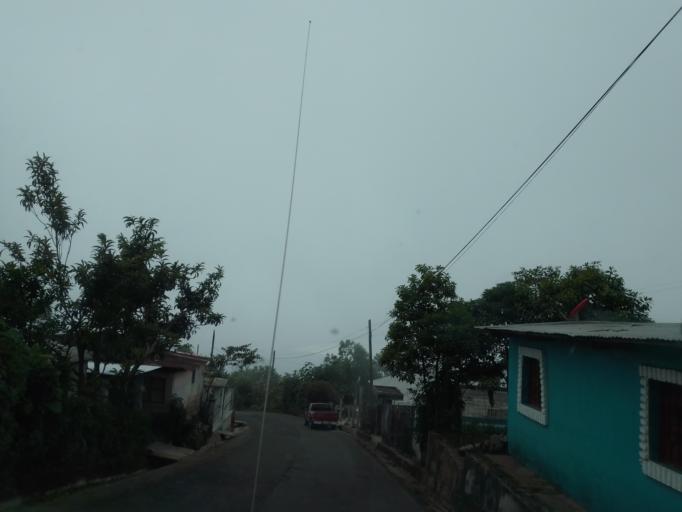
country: MX
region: Chiapas
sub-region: Union Juarez
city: Santo Domingo
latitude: 15.0842
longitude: -92.0837
